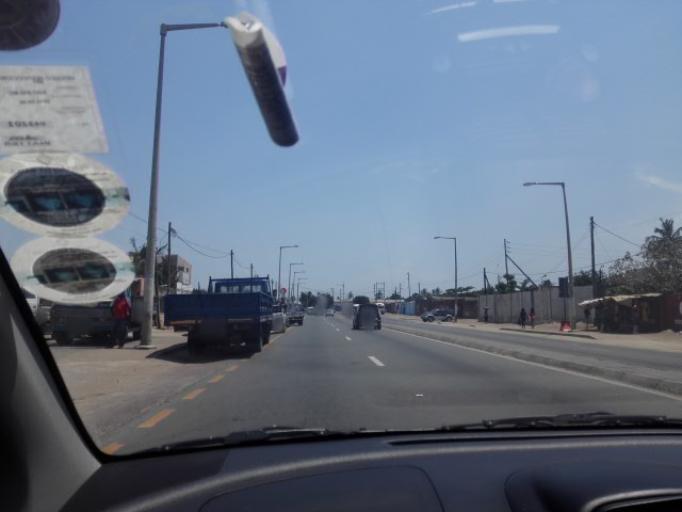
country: MZ
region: Maputo City
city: Maputo
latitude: -25.9066
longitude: 32.5657
